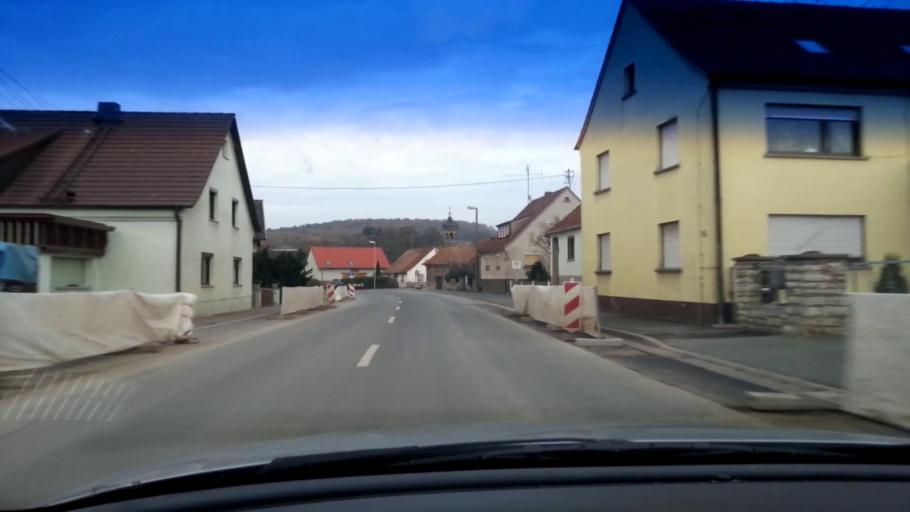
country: DE
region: Bavaria
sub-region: Upper Franconia
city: Breitengussbach
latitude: 49.9793
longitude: 10.8940
